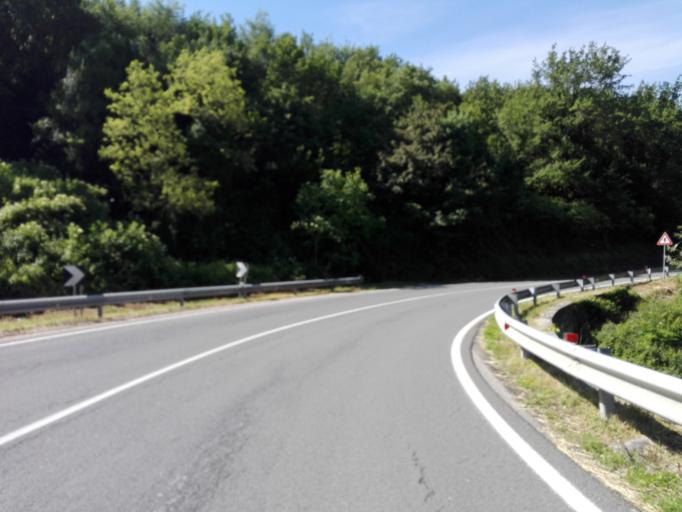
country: IT
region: Umbria
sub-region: Provincia di Perugia
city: Foligno
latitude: 42.9632
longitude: 12.7458
